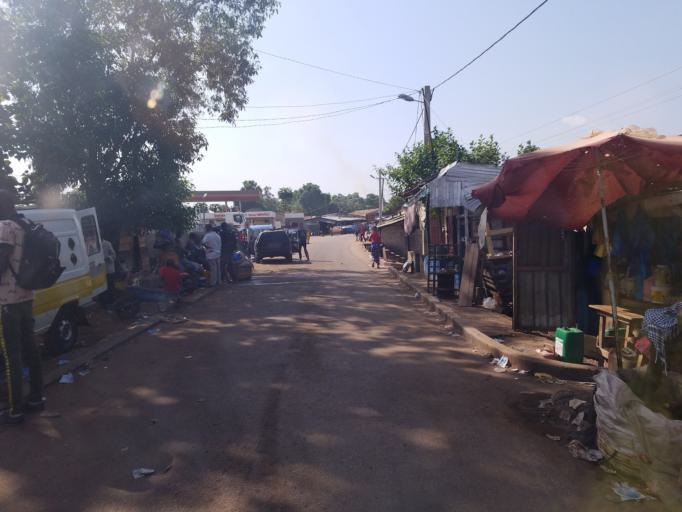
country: GN
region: Boke
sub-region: Fria
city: Fria
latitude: 10.0820
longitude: -13.6909
